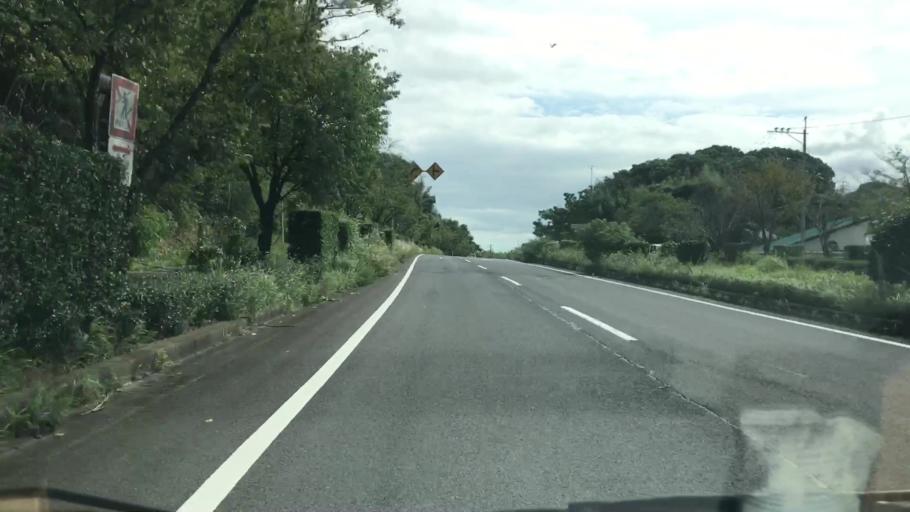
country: JP
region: Saga Prefecture
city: Saga-shi
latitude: 33.2298
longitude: 130.1803
